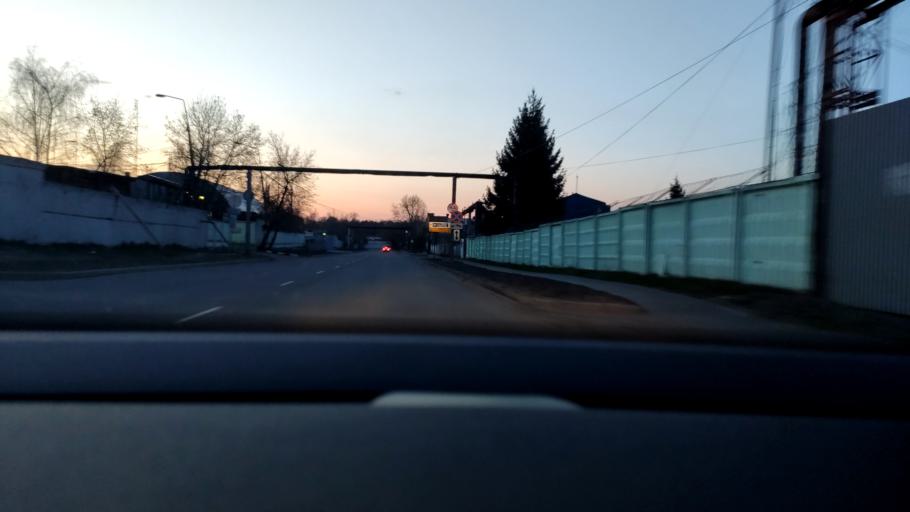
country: RU
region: Moskovskaya
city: Reutov
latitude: 55.7692
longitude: 37.8798
